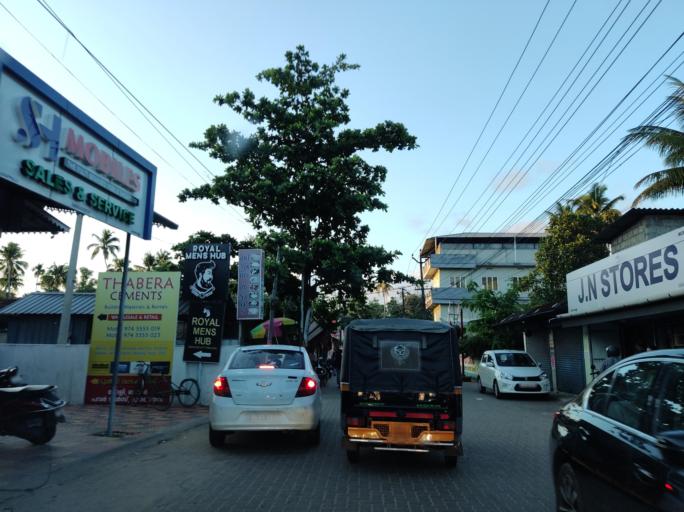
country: IN
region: Kerala
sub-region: Alappuzha
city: Vayalar
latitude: 9.7048
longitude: 76.3028
